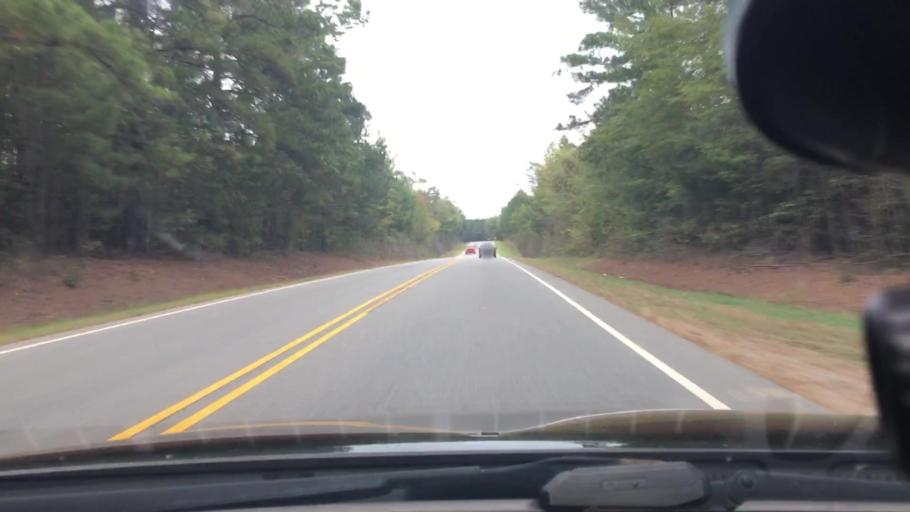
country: US
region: North Carolina
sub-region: Montgomery County
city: Biscoe
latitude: 35.3635
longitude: -79.6871
